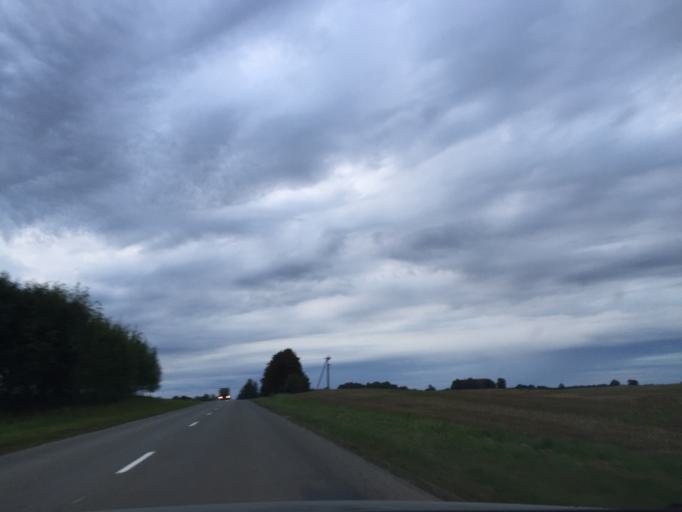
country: LV
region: Vecumnieki
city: Vecumnieki
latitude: 56.4934
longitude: 24.5773
